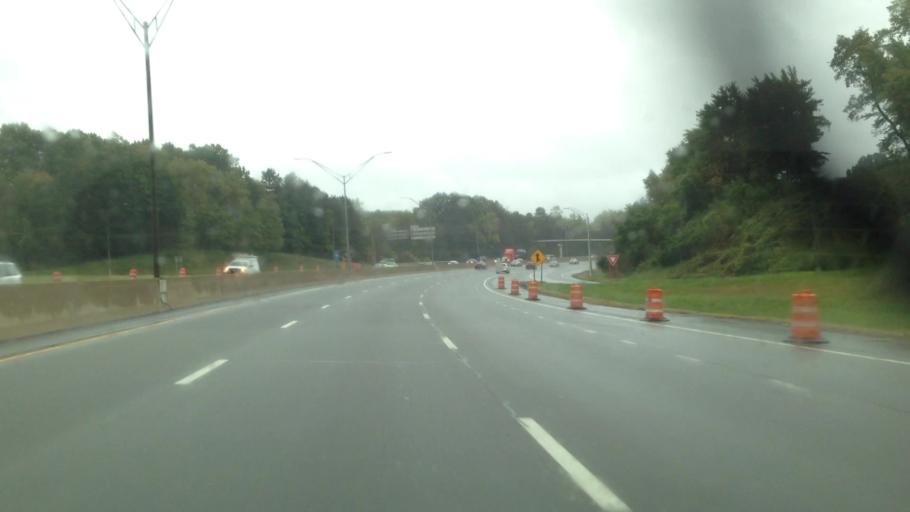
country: US
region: Ohio
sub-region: Summit County
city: Silver Lake
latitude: 41.1625
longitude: -81.4711
